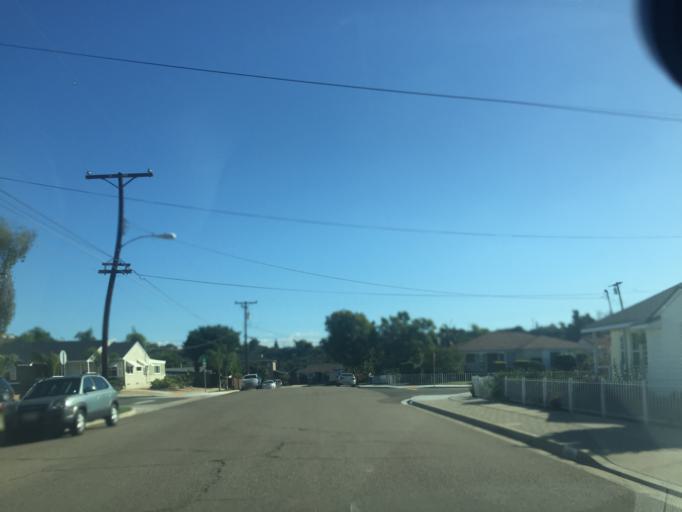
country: US
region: California
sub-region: San Diego County
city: La Mesa
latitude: 32.7915
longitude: -117.0790
